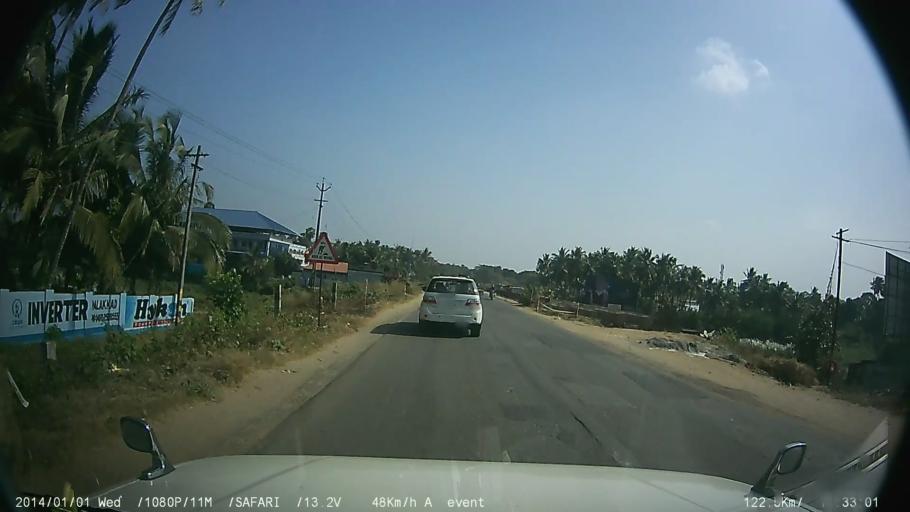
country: IN
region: Kerala
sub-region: Palakkad district
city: Palakkad
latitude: 10.6483
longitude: 76.5614
